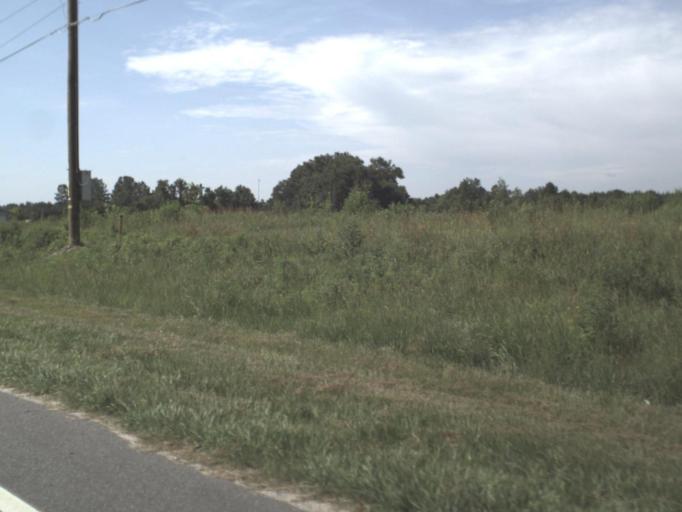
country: US
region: Florida
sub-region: Madison County
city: Madison
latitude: 30.4044
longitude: -83.3634
